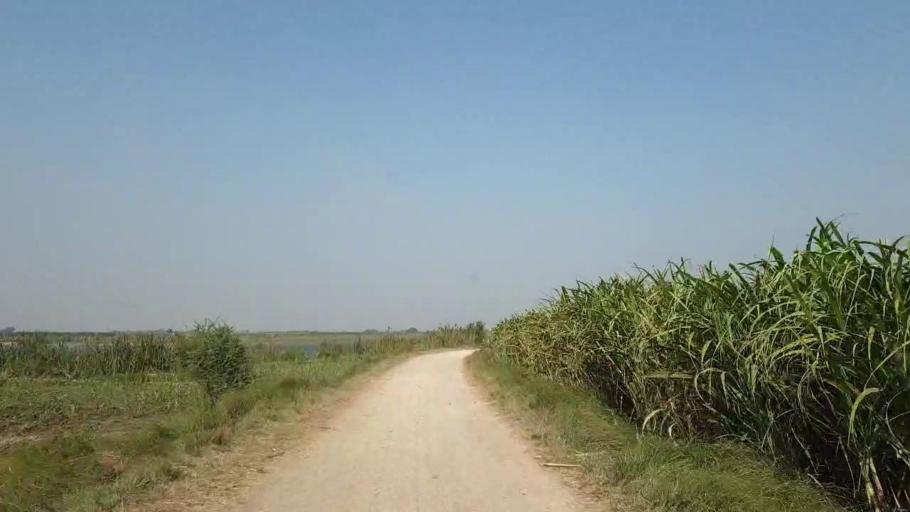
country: PK
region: Sindh
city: Bulri
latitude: 24.9328
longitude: 68.3820
